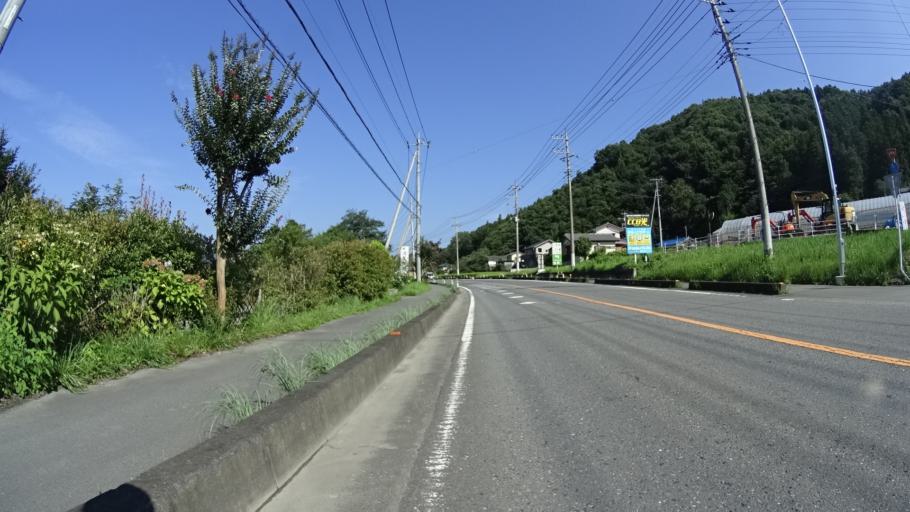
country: JP
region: Saitama
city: Chichibu
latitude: 36.0145
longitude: 139.0204
